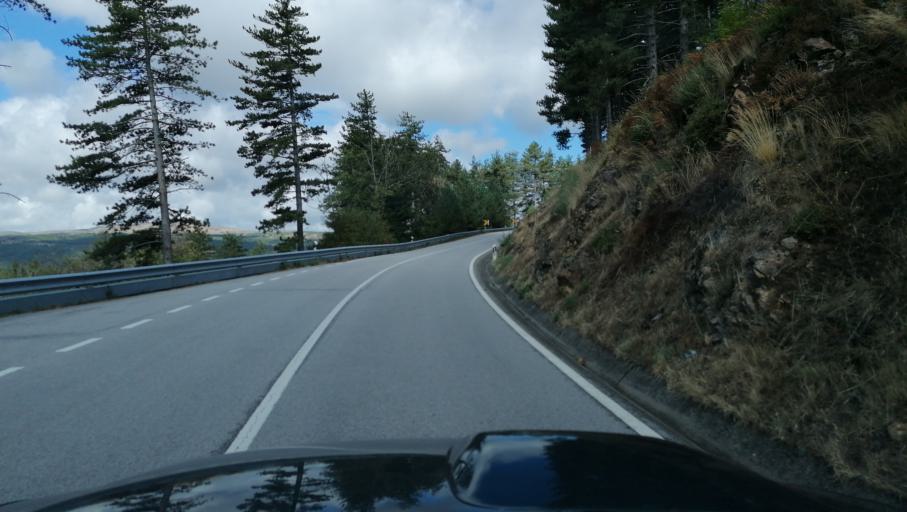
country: PT
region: Vila Real
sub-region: Vila Pouca de Aguiar
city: Vila Pouca de Aguiar
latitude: 41.5074
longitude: -7.6224
